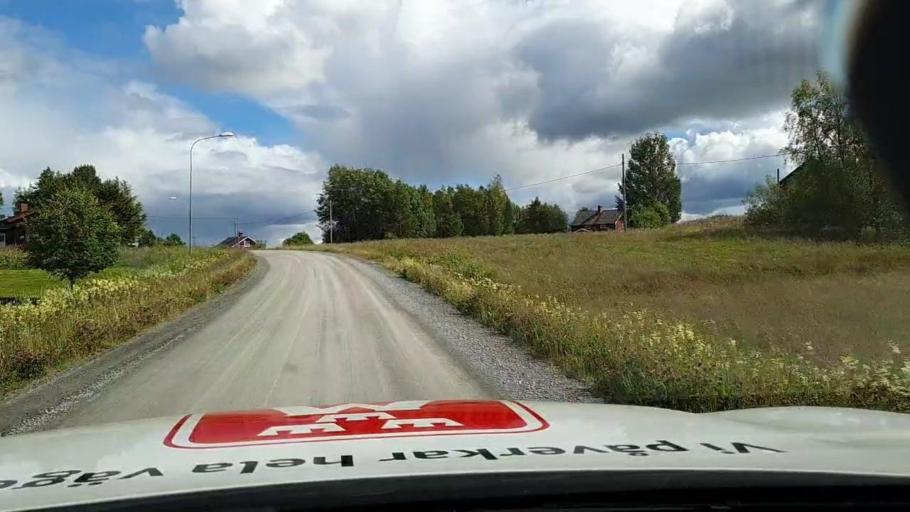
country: SE
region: Jaemtland
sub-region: Krokoms Kommun
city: Valla
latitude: 63.7001
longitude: 13.6014
